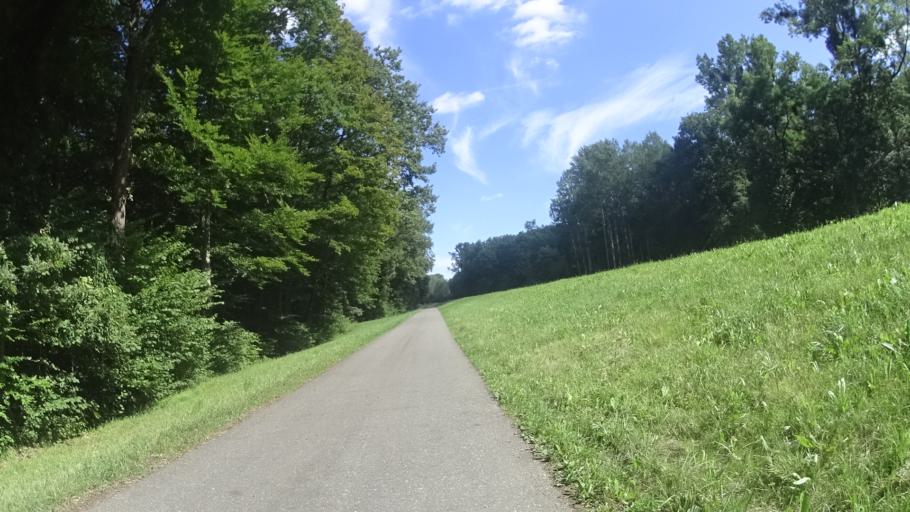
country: DE
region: Rheinland-Pfalz
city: Leimersheim
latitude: 49.1609
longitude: 8.3612
